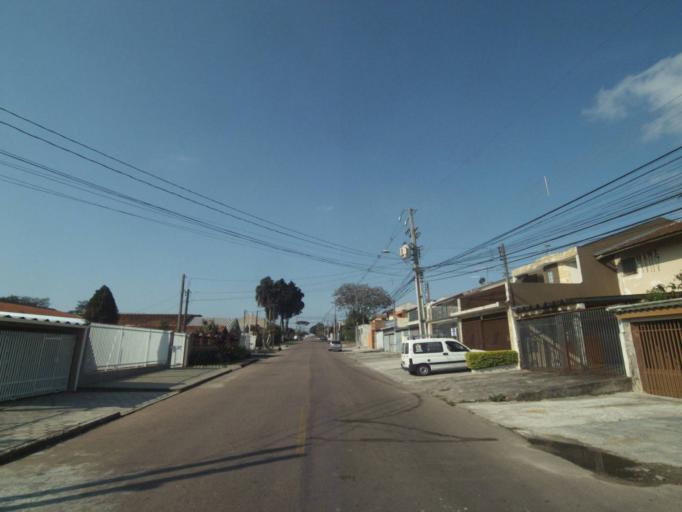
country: BR
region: Parana
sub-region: Curitiba
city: Curitiba
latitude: -25.4890
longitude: -49.3309
